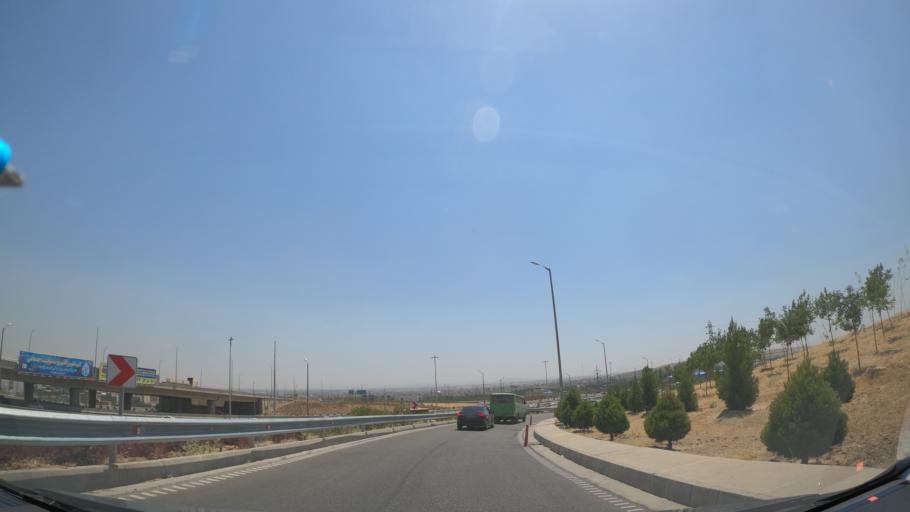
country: IR
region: Tehran
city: Shahr-e Qods
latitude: 35.7436
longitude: 51.1244
